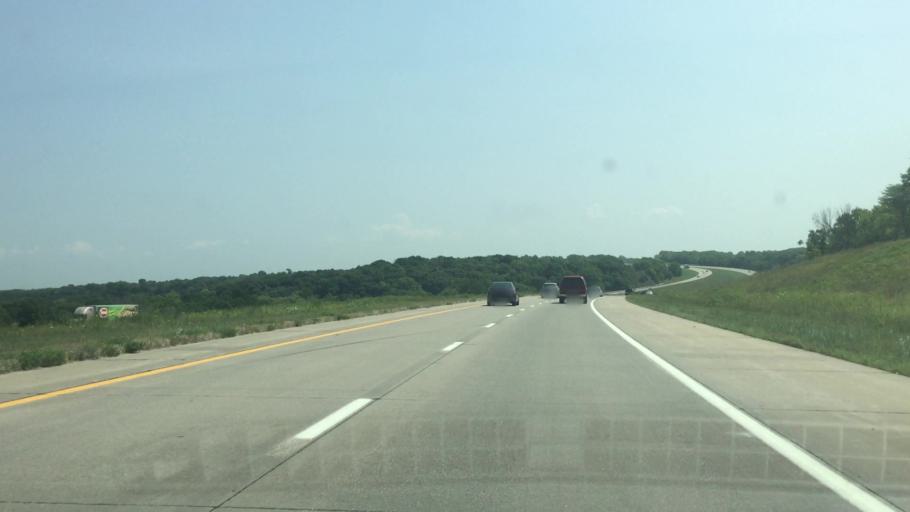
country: US
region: Kansas
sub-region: Osage County
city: Lyndon
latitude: 38.4713
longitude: -95.5276
